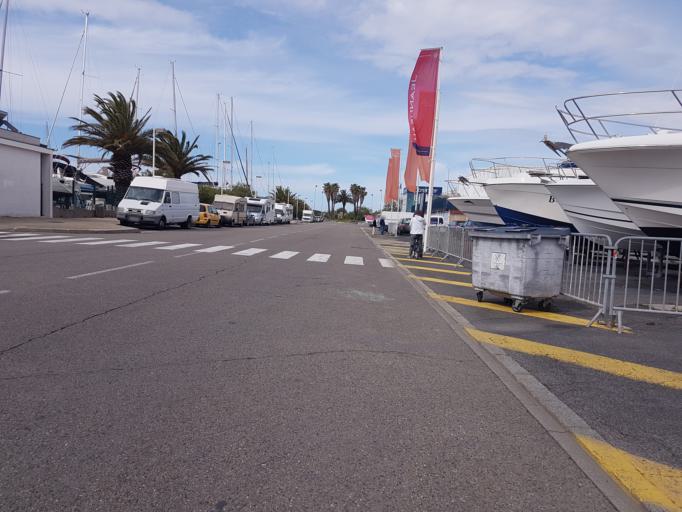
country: FR
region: Languedoc-Roussillon
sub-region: Departement de l'Herault
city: La Grande-Motte
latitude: 43.5591
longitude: 4.0775
